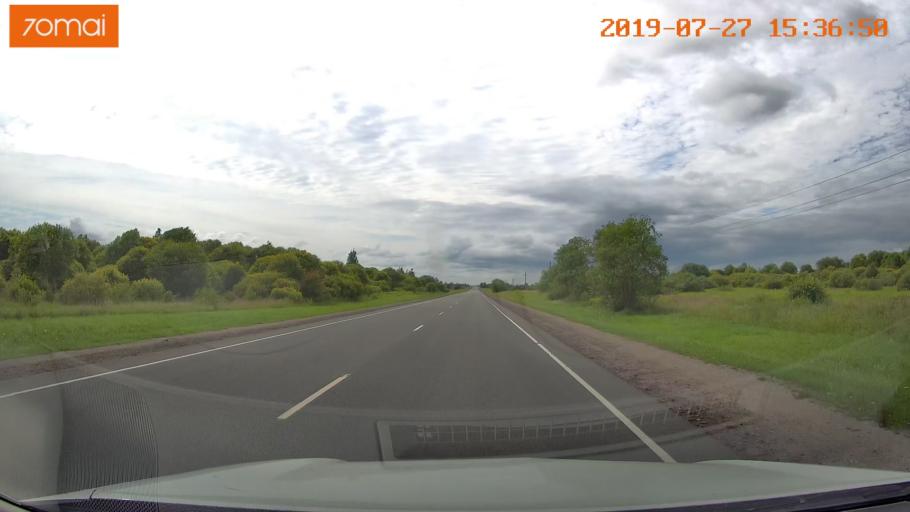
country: RU
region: Kaliningrad
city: Gusev
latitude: 54.6111
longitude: 22.3585
